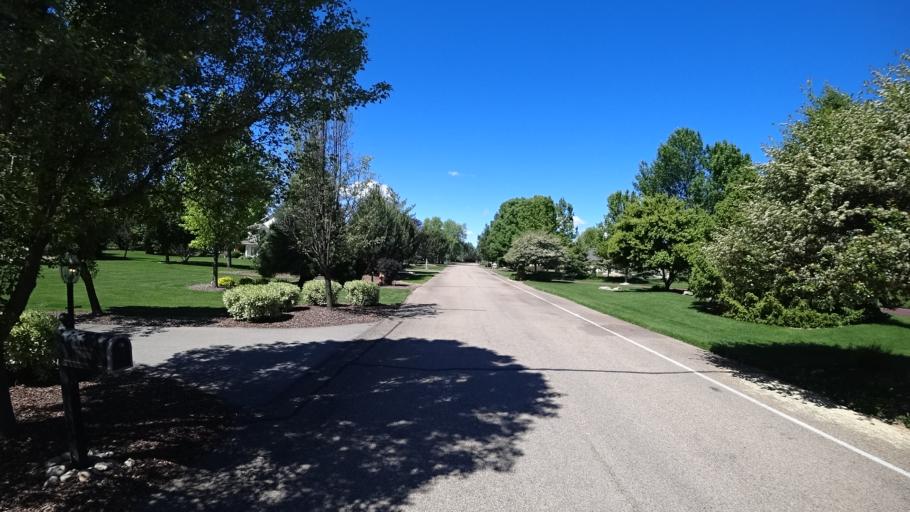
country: US
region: Idaho
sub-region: Ada County
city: Eagle
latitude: 43.6691
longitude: -116.3865
